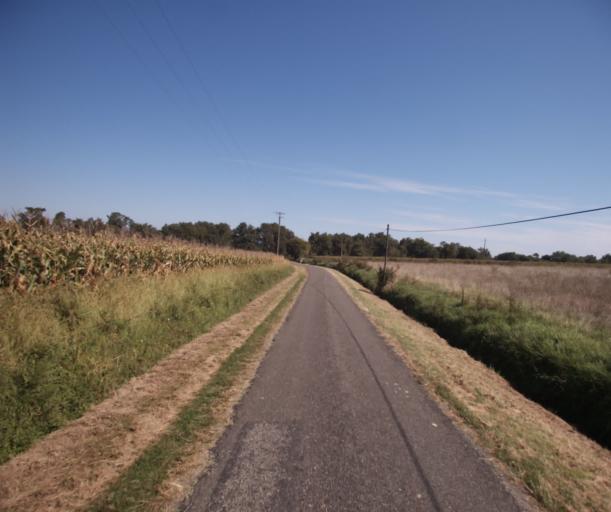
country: FR
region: Aquitaine
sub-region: Departement des Landes
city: Gabarret
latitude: 43.9505
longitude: -0.0107
